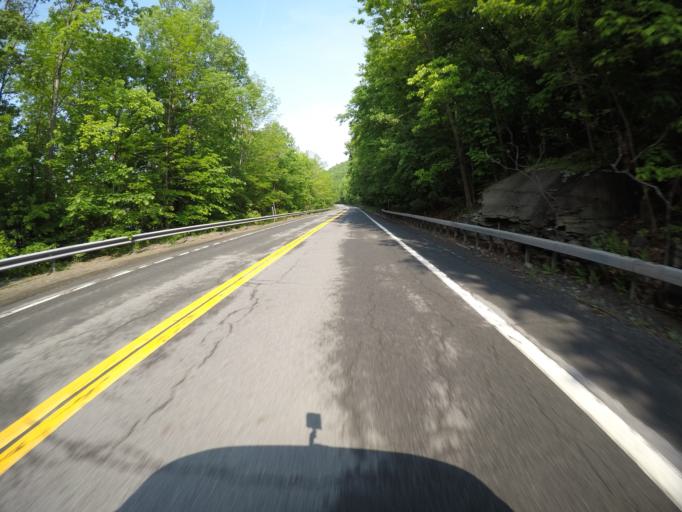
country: US
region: New York
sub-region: Sullivan County
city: Livingston Manor
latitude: 42.0890
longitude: -74.8027
